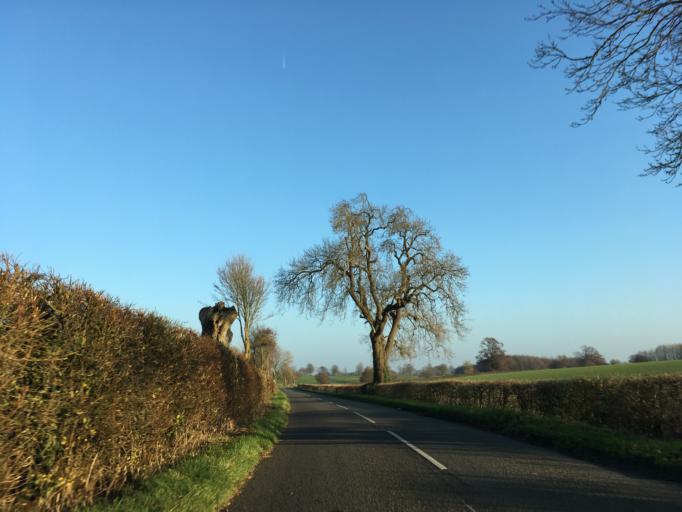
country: GB
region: England
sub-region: Wiltshire
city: Luckington
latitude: 51.5641
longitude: -2.2924
